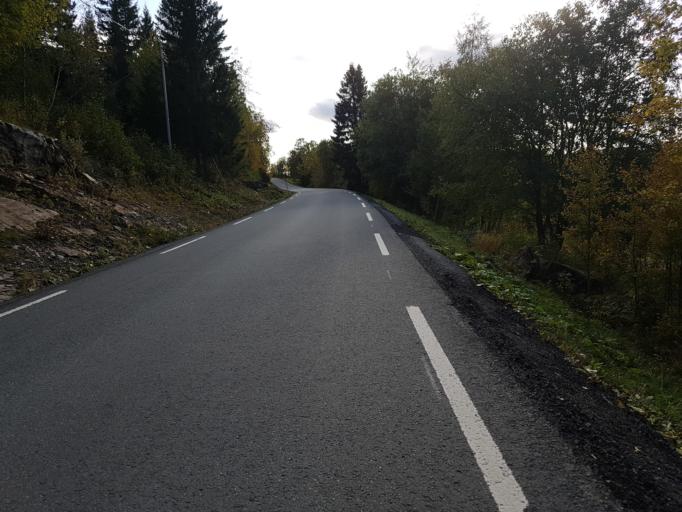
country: NO
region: Sor-Trondelag
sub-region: Malvik
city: Malvik
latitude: 63.3656
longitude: 10.6233
